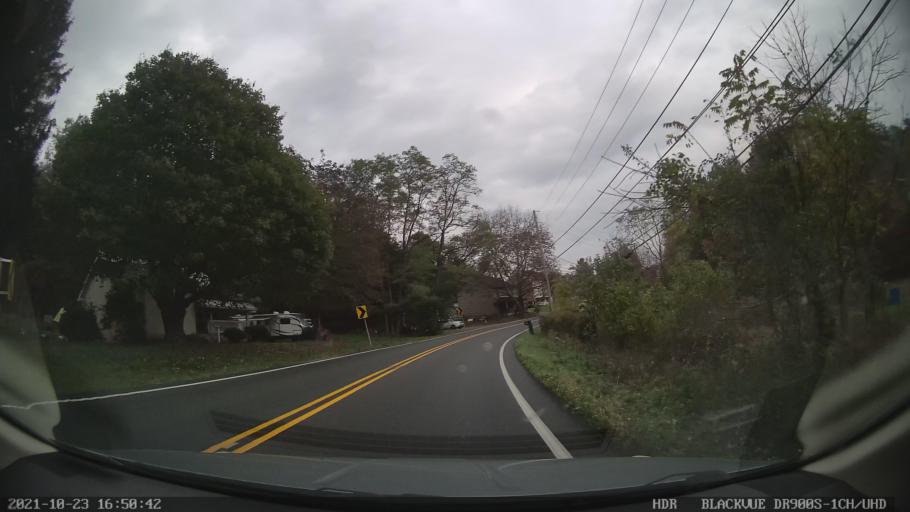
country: US
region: Pennsylvania
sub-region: Berks County
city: Red Lion
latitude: 40.4765
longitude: -75.6123
